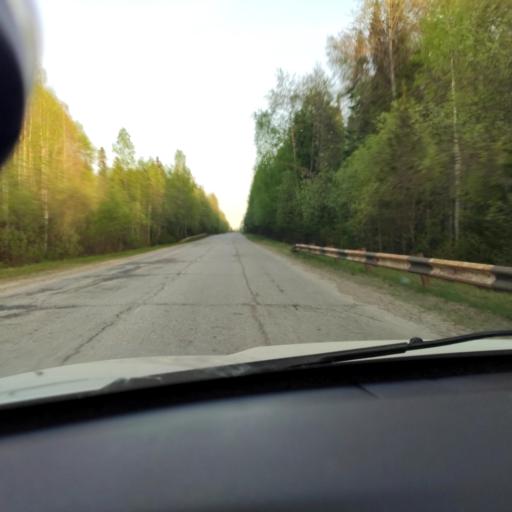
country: RU
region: Perm
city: Dobryanka
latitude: 58.4625
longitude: 56.4819
